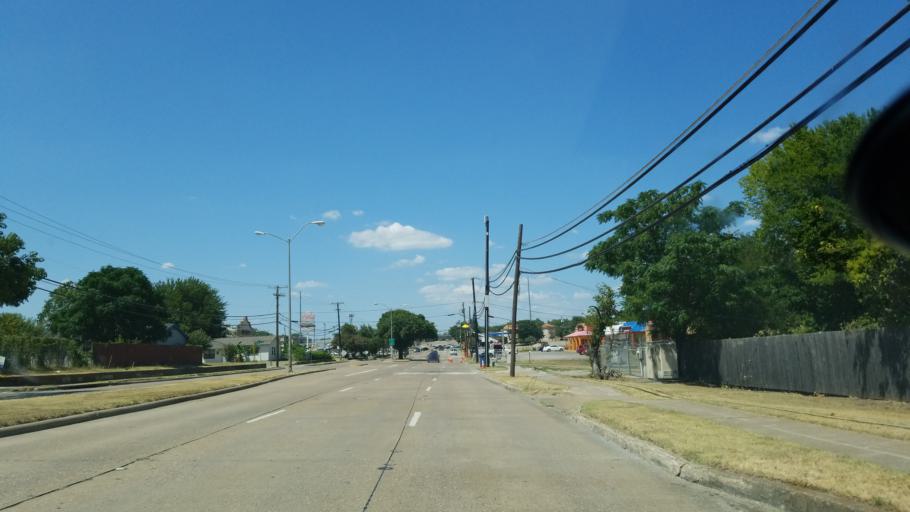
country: US
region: Texas
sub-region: Dallas County
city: Cockrell Hill
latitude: 32.7174
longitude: -96.8913
